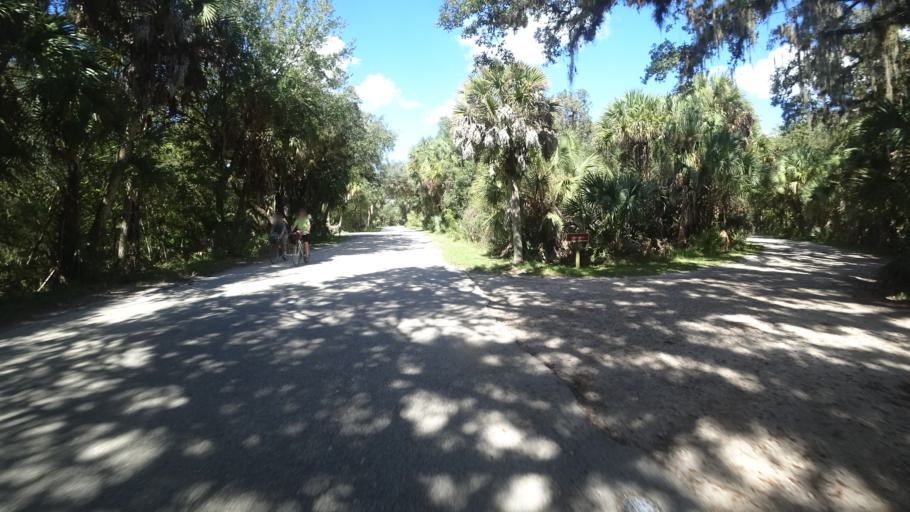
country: US
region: Florida
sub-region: Sarasota County
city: Lake Sarasota
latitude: 27.2429
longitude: -82.3142
